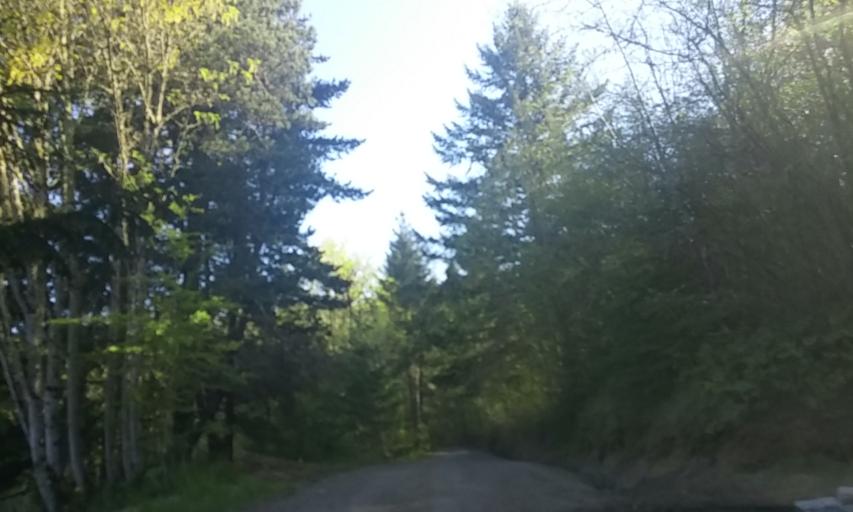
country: US
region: Oregon
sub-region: Washington County
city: Cedar Mill
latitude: 45.5511
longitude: -122.7877
